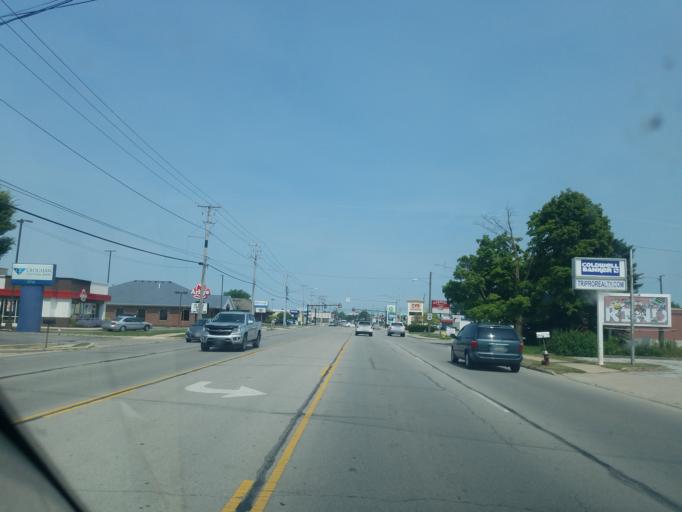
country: US
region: Ohio
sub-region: Seneca County
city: Tiffin
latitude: 41.1110
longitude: -83.2081
